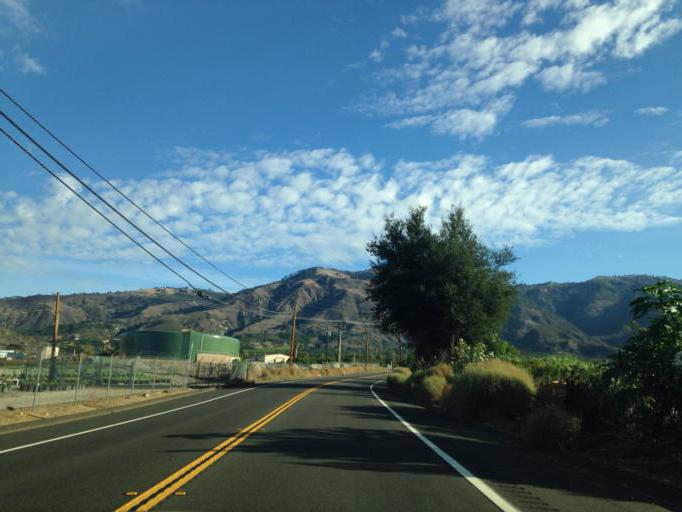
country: US
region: California
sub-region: San Diego County
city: Valley Center
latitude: 33.2925
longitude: -116.9480
